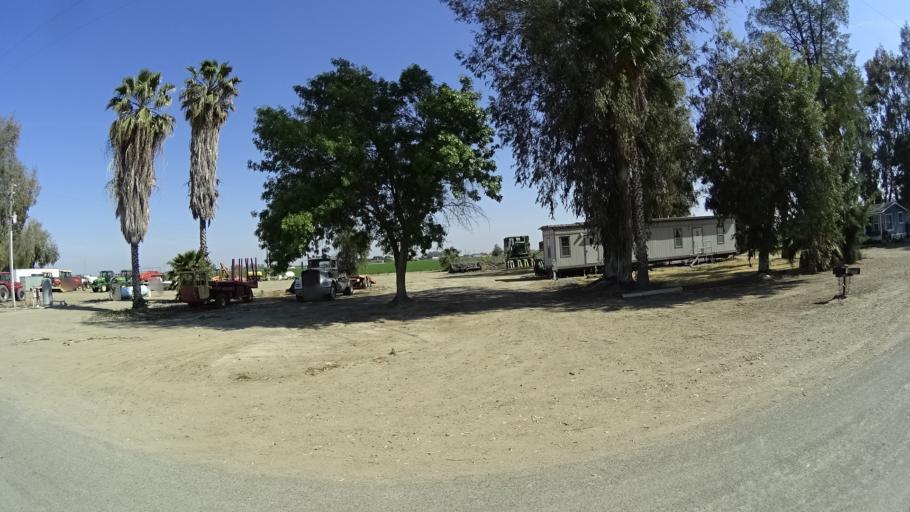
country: US
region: California
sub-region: Fresno County
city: Riverdale
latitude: 36.3512
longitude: -119.8789
